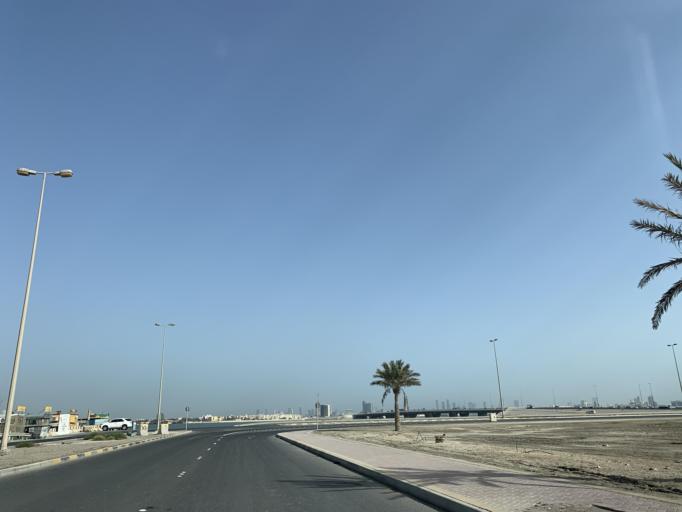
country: BH
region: Northern
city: Sitrah
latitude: 26.1692
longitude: 50.5989
